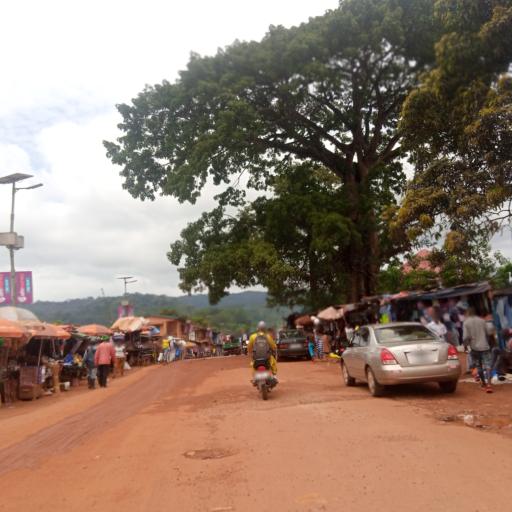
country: SL
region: Eastern Province
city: Kenema
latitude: 7.8744
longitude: -11.1925
